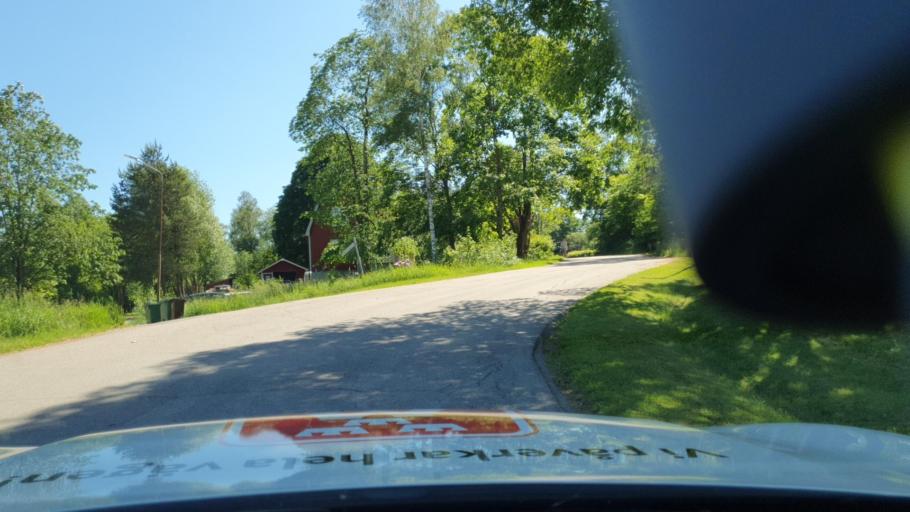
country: SE
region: Vaermland
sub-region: Storfors Kommun
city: Storfors
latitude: 59.5358
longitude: 14.2805
